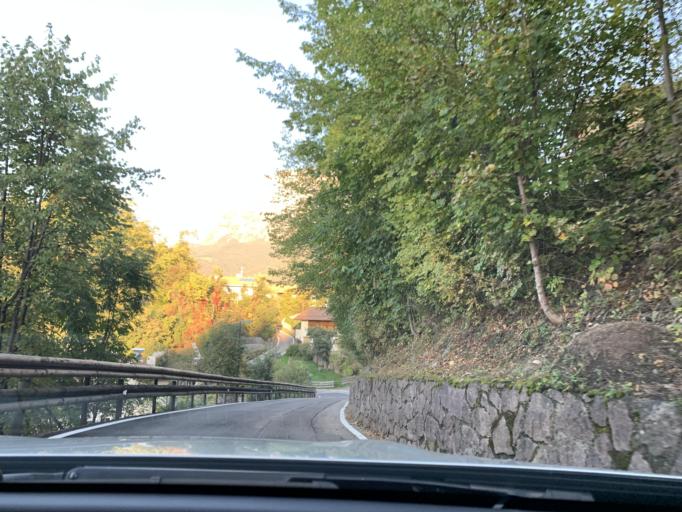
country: IT
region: Trentino-Alto Adige
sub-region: Bolzano
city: Fie Allo Sciliar
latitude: 46.5031
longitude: 11.4962
